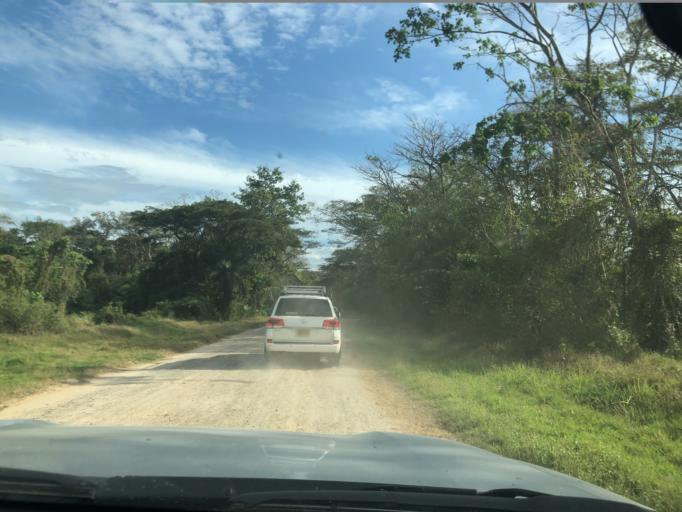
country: CR
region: Alajuela
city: San Jose
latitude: 11.1151
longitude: -85.2830
